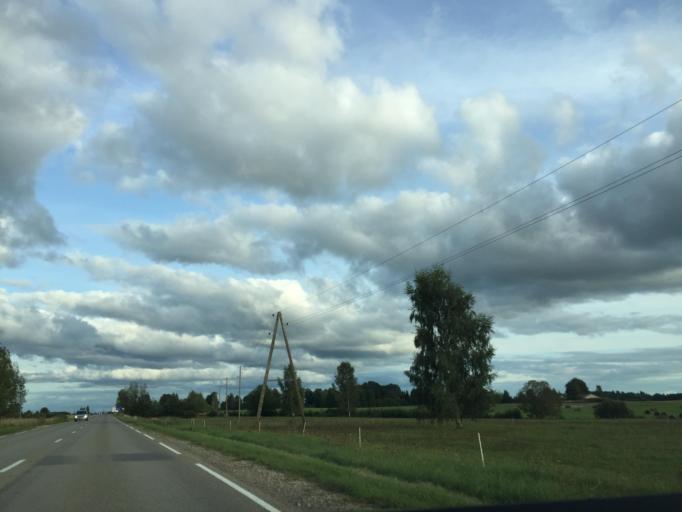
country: LV
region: Nereta
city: Nereta
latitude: 56.2551
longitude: 25.2081
